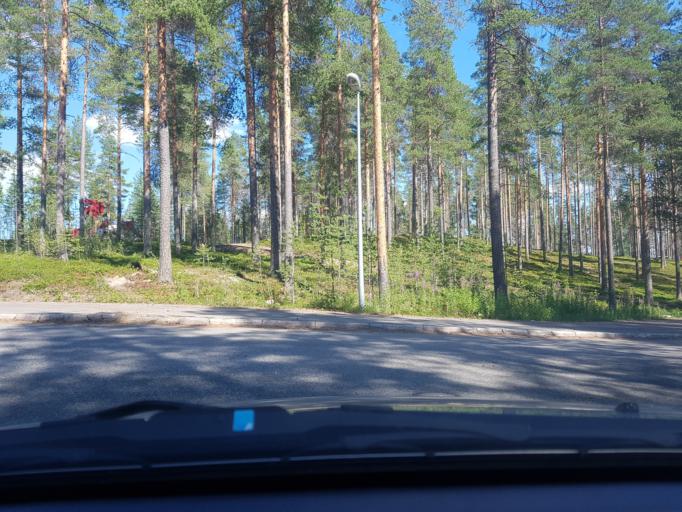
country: FI
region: Kainuu
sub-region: Kehys-Kainuu
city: Kuhmo
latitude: 64.1163
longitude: 29.5862
